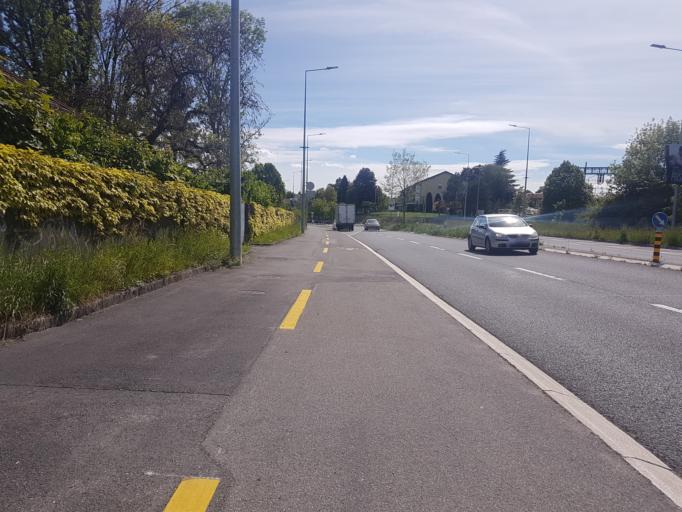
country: CH
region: Geneva
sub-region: Geneva
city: Bellevue
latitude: 46.2587
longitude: 6.1574
